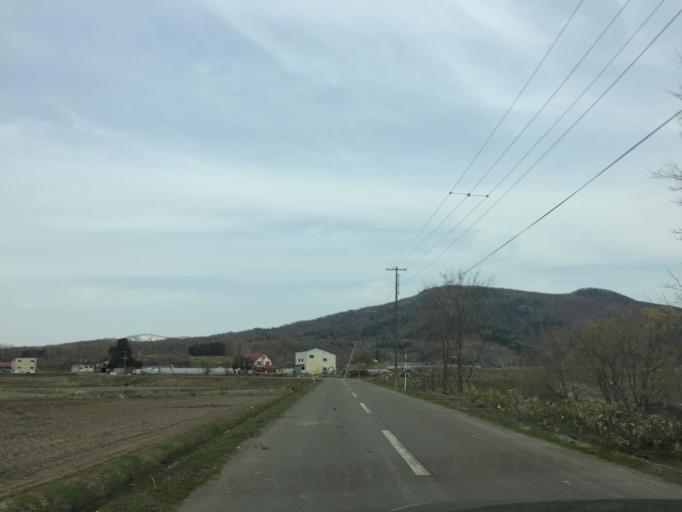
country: JP
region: Hokkaido
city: Ashibetsu
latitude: 43.6152
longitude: 142.2152
